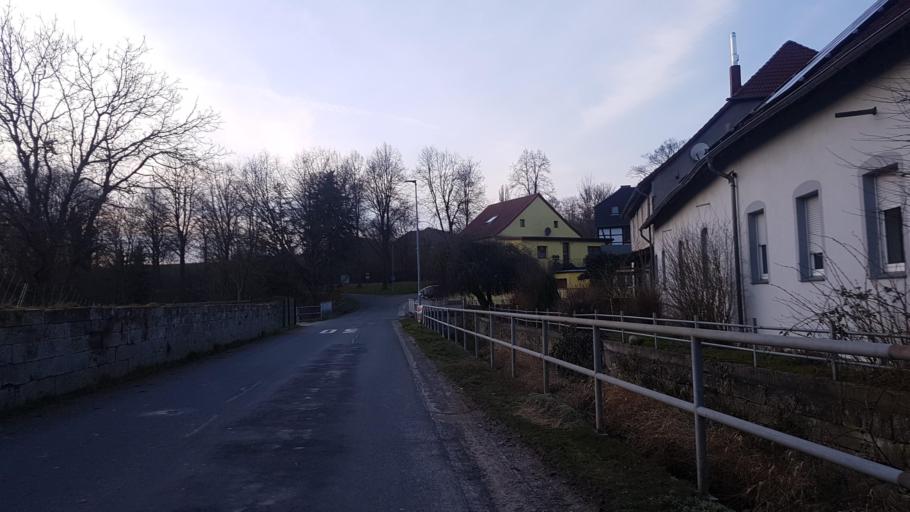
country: DE
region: Lower Saxony
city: Bad Munder am Deister
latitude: 52.1720
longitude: 9.5134
